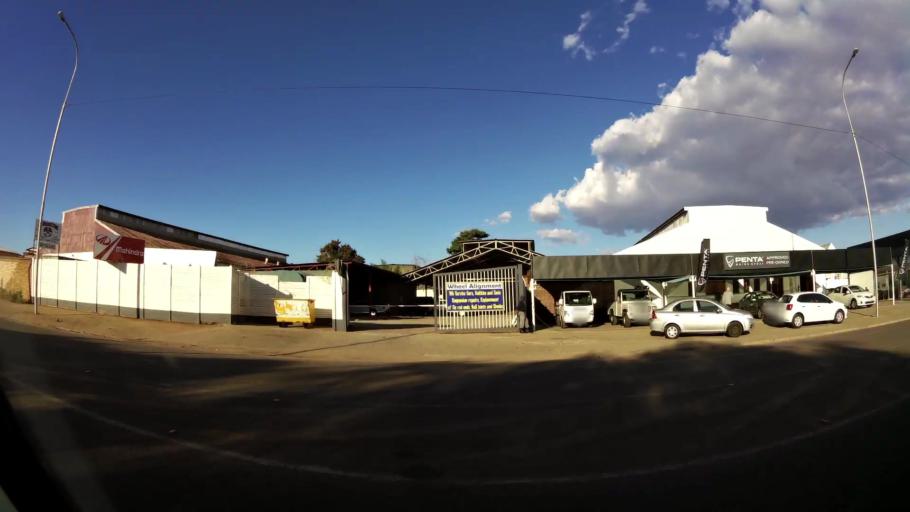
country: ZA
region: Limpopo
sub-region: Waterberg District Municipality
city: Mokopane
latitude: -24.1765
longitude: 29.0020
